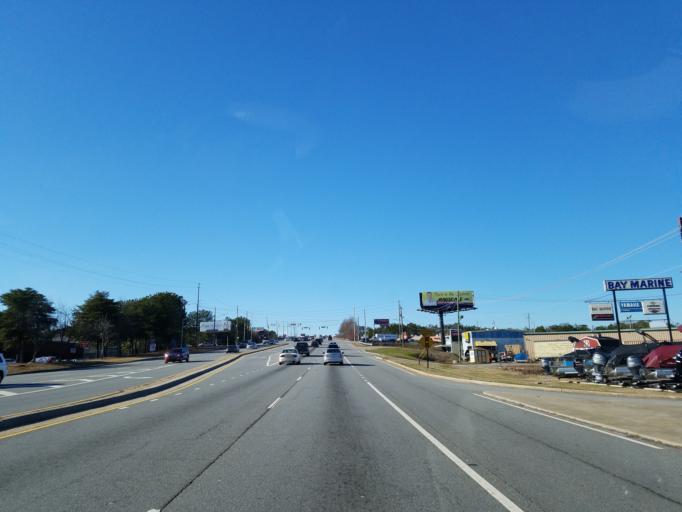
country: US
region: Georgia
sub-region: Cobb County
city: Kennesaw
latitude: 34.0102
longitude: -84.6091
